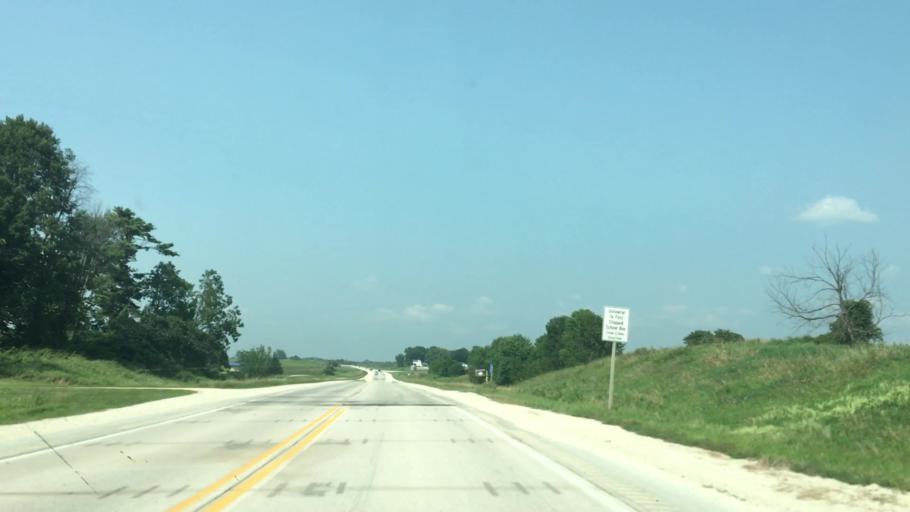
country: US
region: Iowa
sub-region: Winneshiek County
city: Decorah
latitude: 43.3484
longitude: -91.8056
